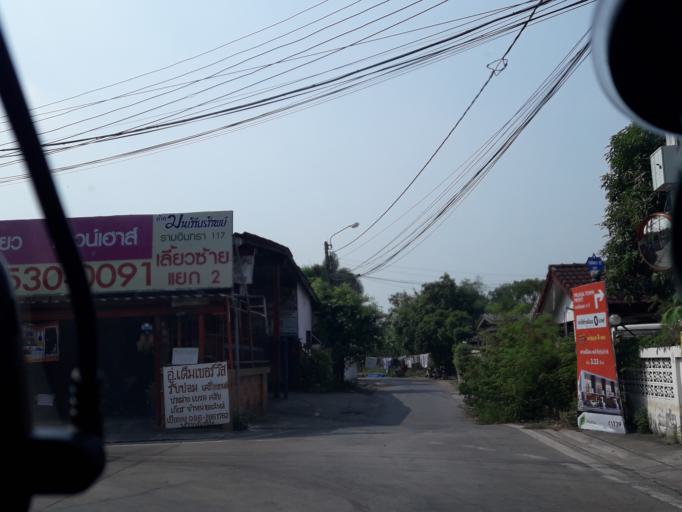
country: TH
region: Bangkok
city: Khan Na Yao
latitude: 13.8187
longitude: 100.7040
